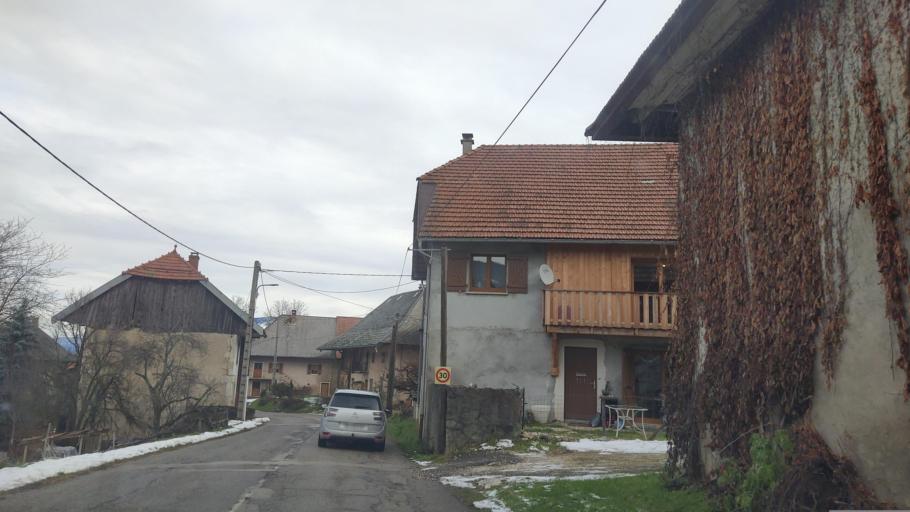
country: FR
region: Rhone-Alpes
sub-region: Departement de la Haute-Savoie
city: Cusy
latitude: 45.6736
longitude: 6.0562
